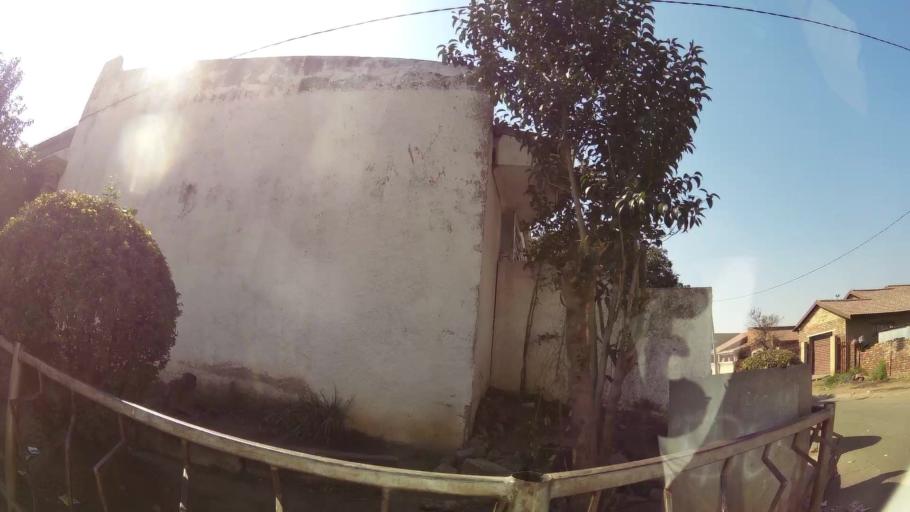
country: ZA
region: Gauteng
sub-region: Ekurhuleni Metropolitan Municipality
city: Boksburg
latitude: -26.2227
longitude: 28.2959
